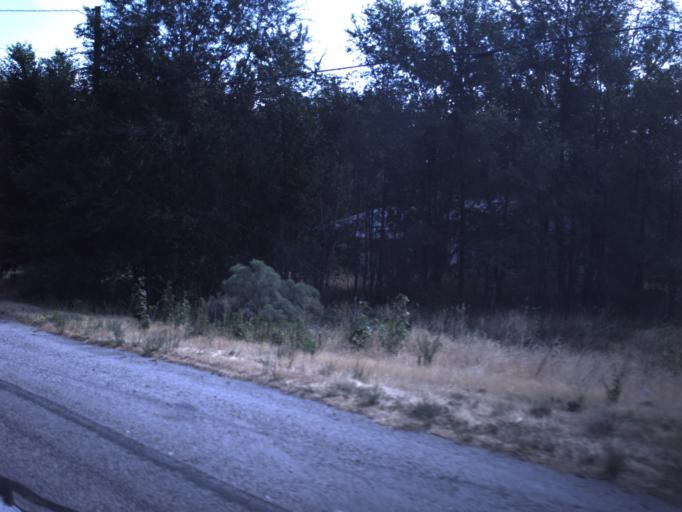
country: US
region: Utah
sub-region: Box Elder County
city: Willard
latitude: 41.3972
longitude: -112.0344
